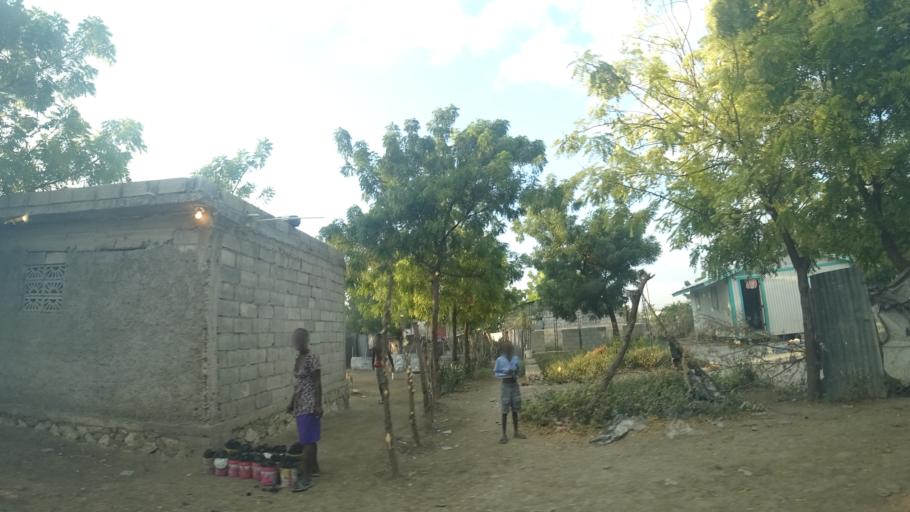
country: HT
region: Ouest
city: Croix des Bouquets
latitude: 18.6504
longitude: -72.2810
